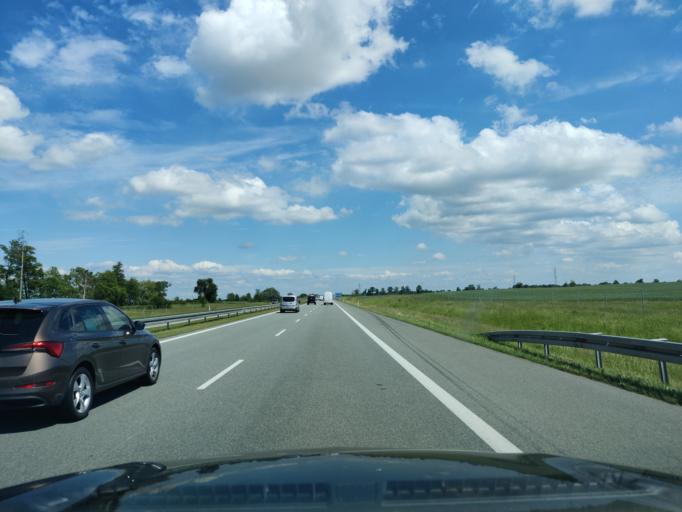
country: PL
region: Greater Poland Voivodeship
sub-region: Powiat wrzesinski
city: Wrzesnia
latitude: 52.3190
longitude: 17.4879
